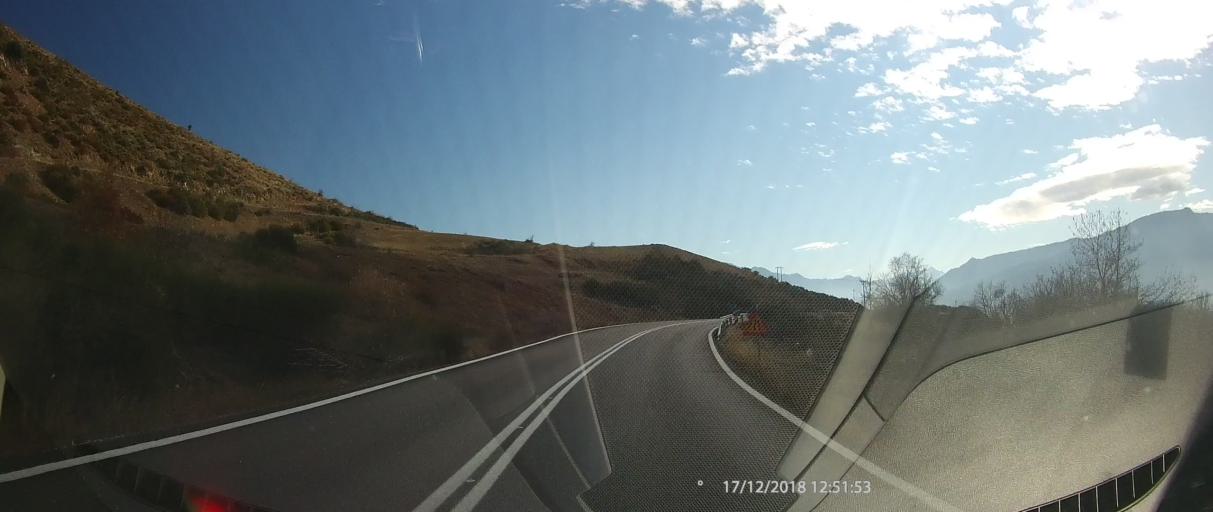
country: GR
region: Thessaly
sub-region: Trikala
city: Kastraki
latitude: 39.7617
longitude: 21.4731
